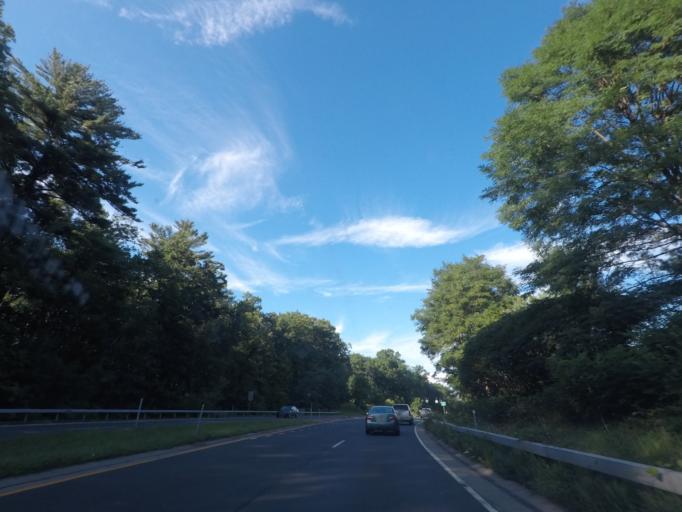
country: US
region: New York
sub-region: Schenectady County
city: Niskayuna
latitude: 42.7531
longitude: -73.8197
